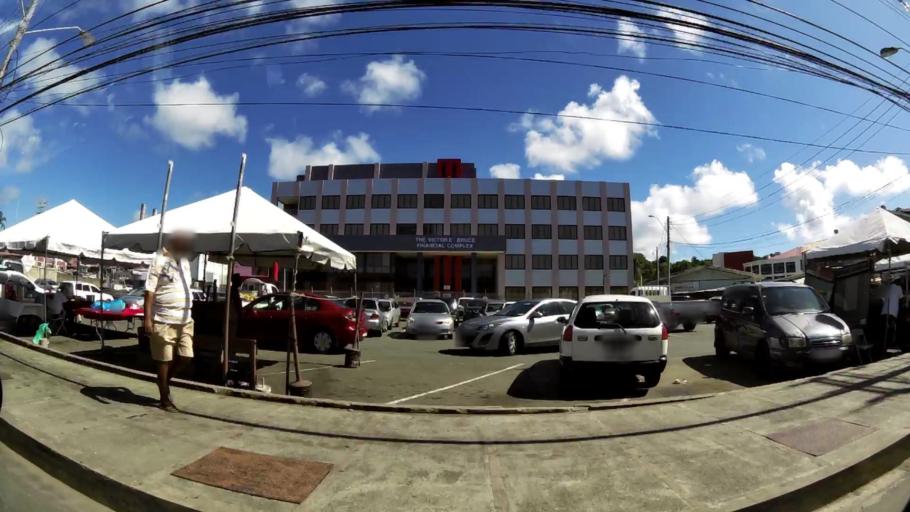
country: TT
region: Tobago
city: Scarborough
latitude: 11.1842
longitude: -60.7378
